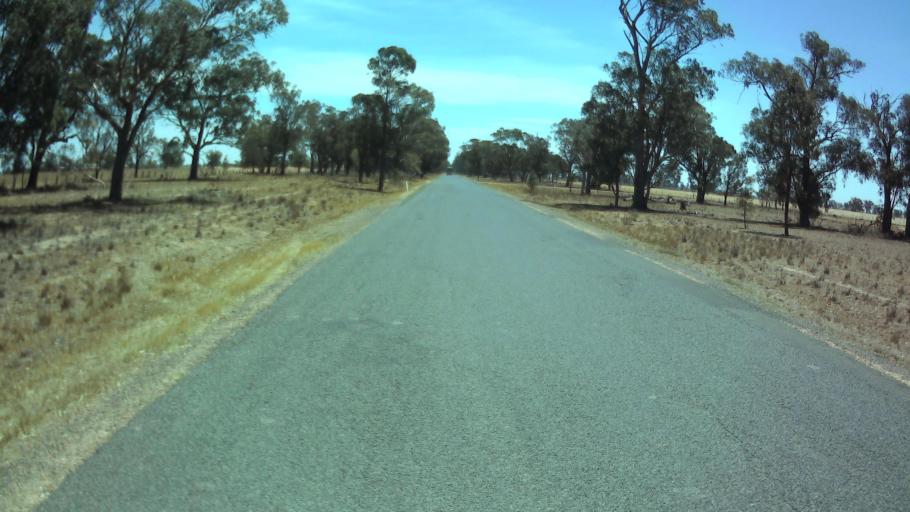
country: AU
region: New South Wales
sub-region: Weddin
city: Grenfell
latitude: -34.0048
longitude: 147.7677
